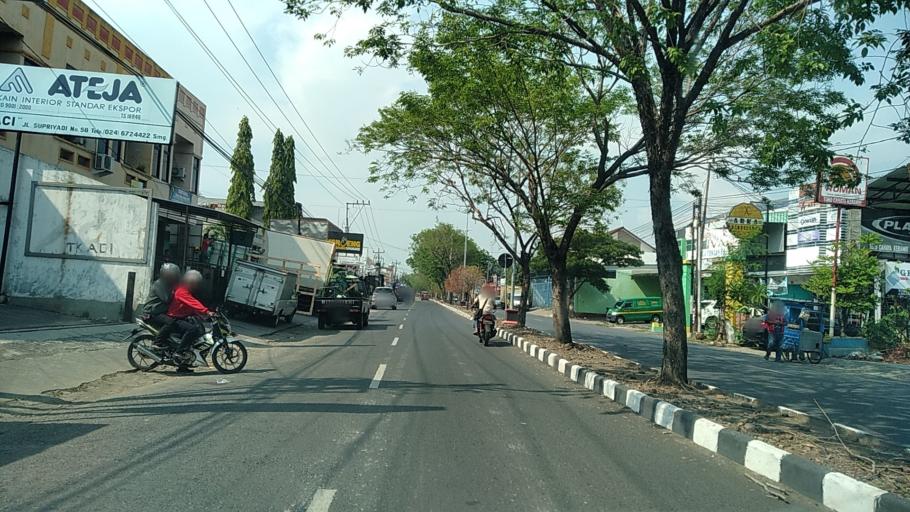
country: ID
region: Central Java
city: Semarang
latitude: -7.0010
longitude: 110.4555
